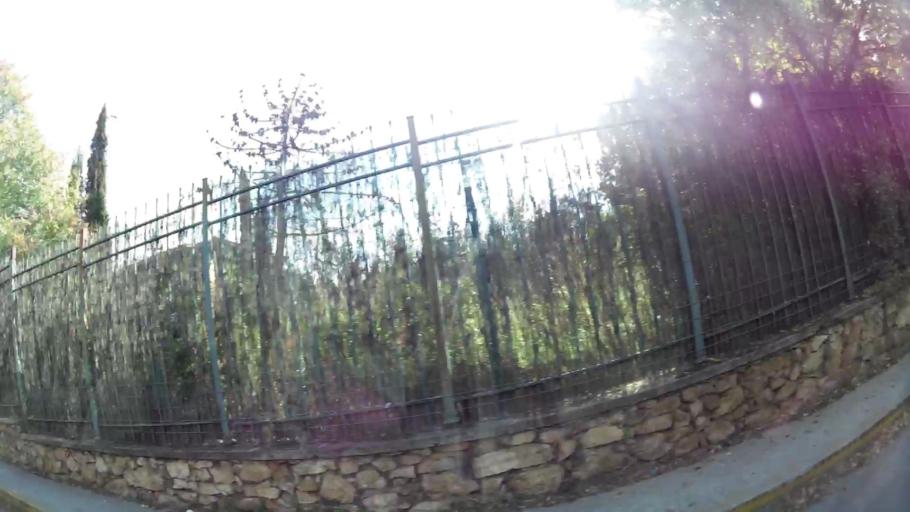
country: GR
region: Attica
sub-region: Nomarchia Athinas
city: Melissia
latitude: 38.0573
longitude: 23.8197
